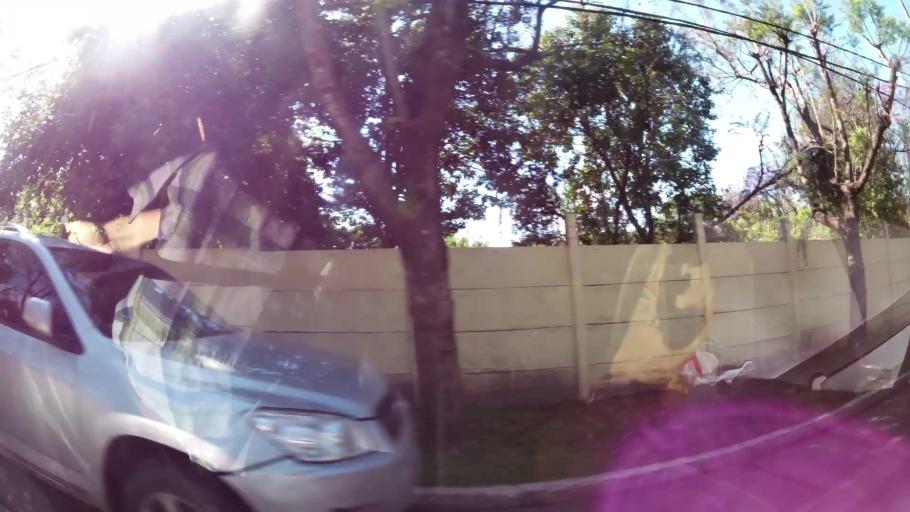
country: AR
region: Buenos Aires
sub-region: Partido de Tigre
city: Tigre
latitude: -34.4862
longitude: -58.5781
